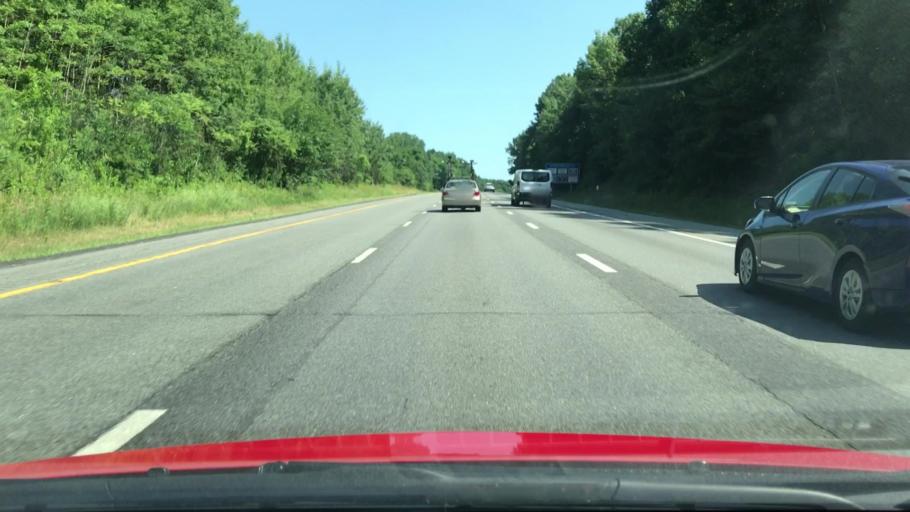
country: US
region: New York
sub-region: Saratoga County
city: Ballston Spa
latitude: 43.0076
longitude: -73.8010
